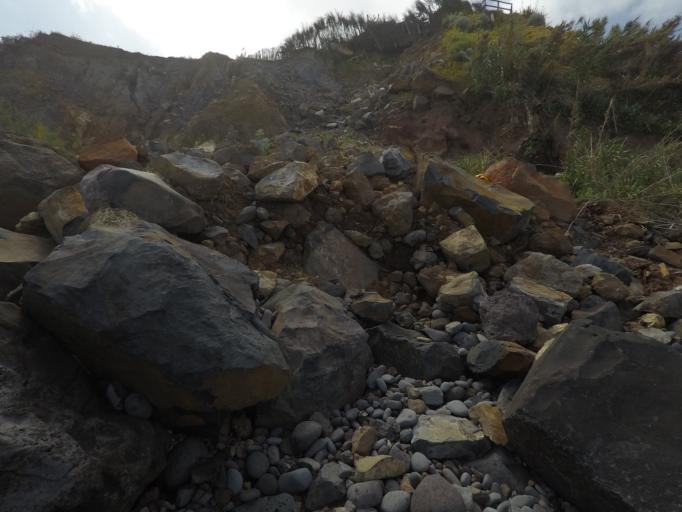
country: PT
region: Madeira
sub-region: Sao Vicente
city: Sao Vicente
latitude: 32.8241
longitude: -16.9974
